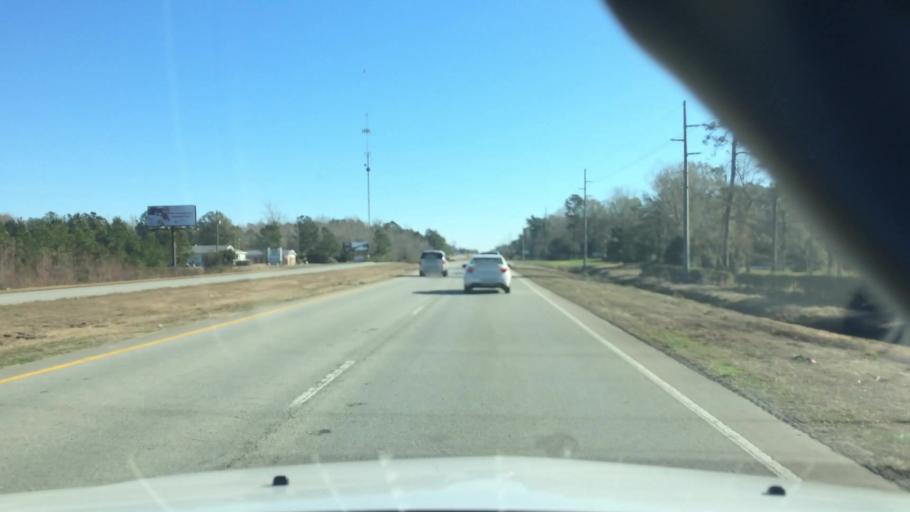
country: US
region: North Carolina
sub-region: Brunswick County
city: Sunset Beach
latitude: 33.9473
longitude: -78.4961
